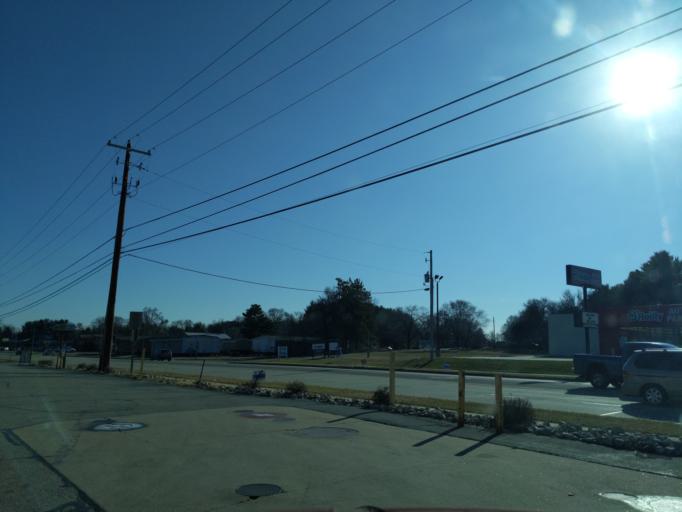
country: US
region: Wisconsin
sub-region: Waushara County
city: Wautoma
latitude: 44.0685
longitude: -89.2668
